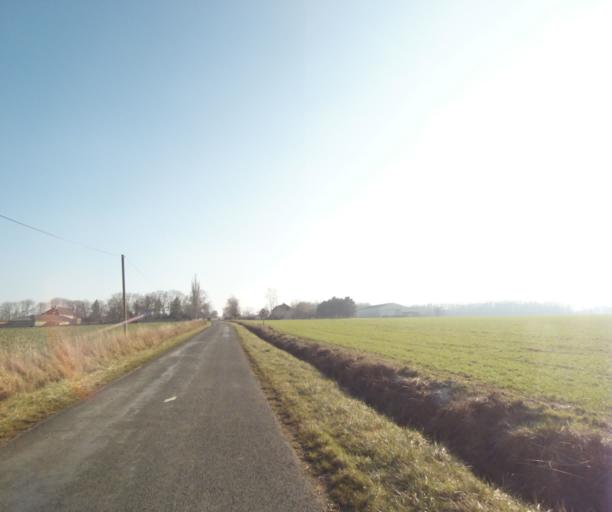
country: FR
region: Champagne-Ardenne
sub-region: Departement de la Haute-Marne
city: Chevillon
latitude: 48.4944
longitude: 5.0614
